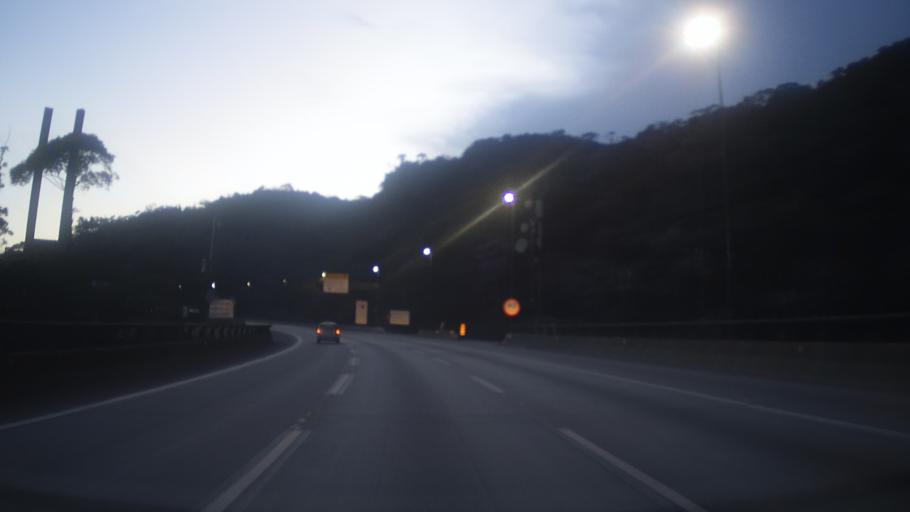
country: BR
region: Sao Paulo
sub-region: Cubatao
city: Cubatao
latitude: -23.9185
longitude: -46.5291
